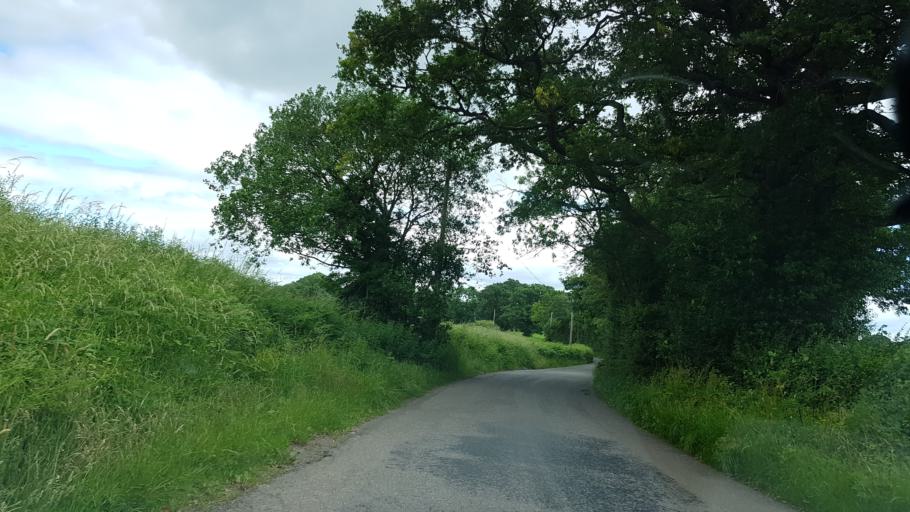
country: GB
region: Wales
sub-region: Monmouthshire
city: Llanarth
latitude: 51.7746
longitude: -2.8355
